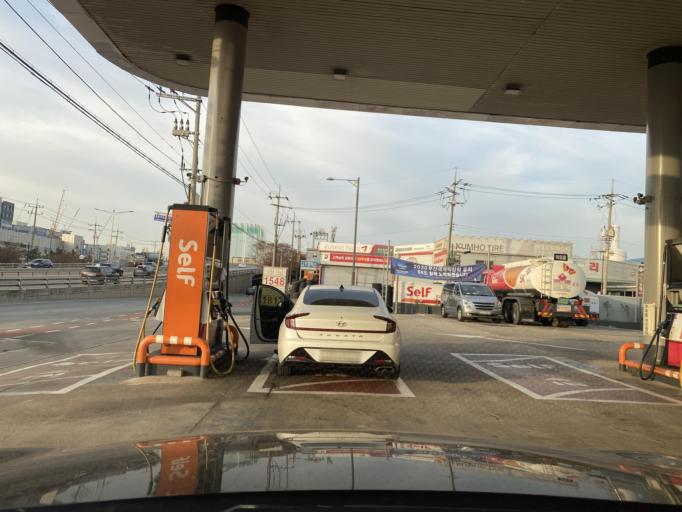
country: KR
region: Incheon
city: Incheon
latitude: 37.5043
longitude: 126.6487
